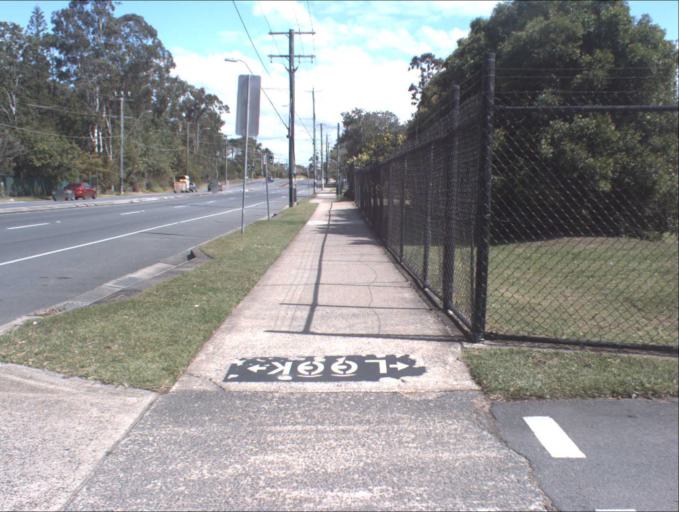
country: AU
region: Queensland
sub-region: Logan
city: Waterford West
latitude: -27.6873
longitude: 153.1060
